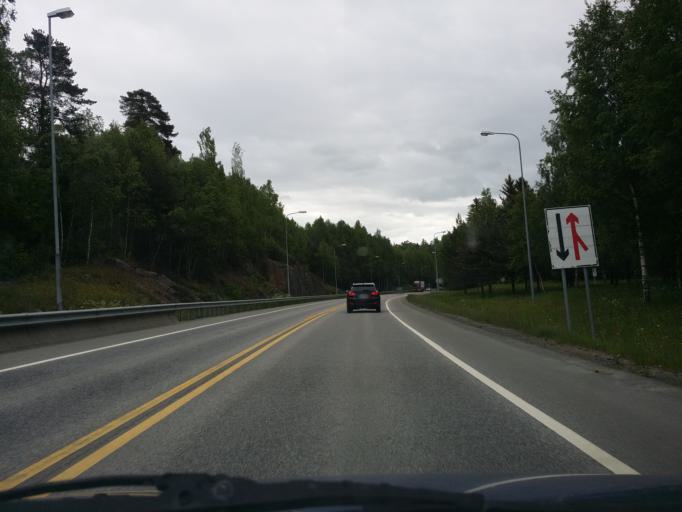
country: NO
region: Hedmark
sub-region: Ringsaker
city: Moelv
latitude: 60.9180
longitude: 10.7089
